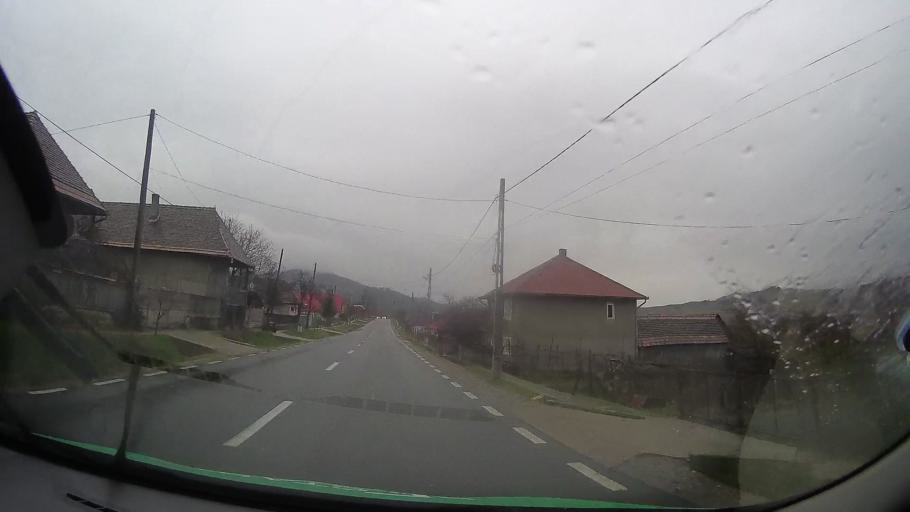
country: RO
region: Bistrita-Nasaud
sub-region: Comuna Galatii Bistritei
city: Galatii Bistritei
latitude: 46.9883
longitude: 24.4241
